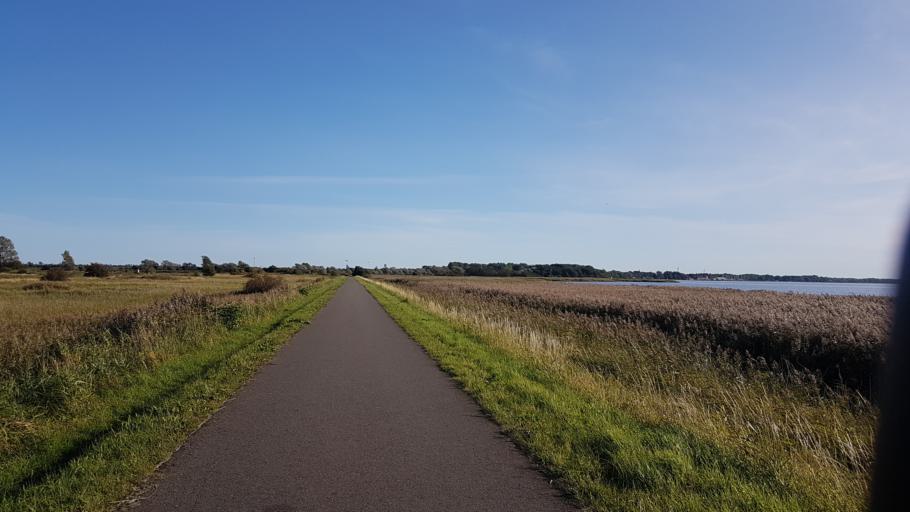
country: DE
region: Mecklenburg-Vorpommern
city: Wiek
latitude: 54.6439
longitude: 13.2860
